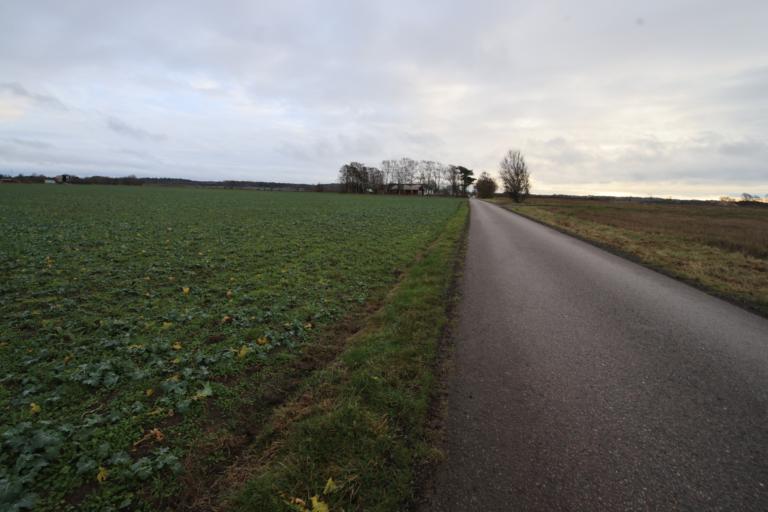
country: SE
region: Halland
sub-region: Varbergs Kommun
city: Traslovslage
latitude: 57.0878
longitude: 12.2914
